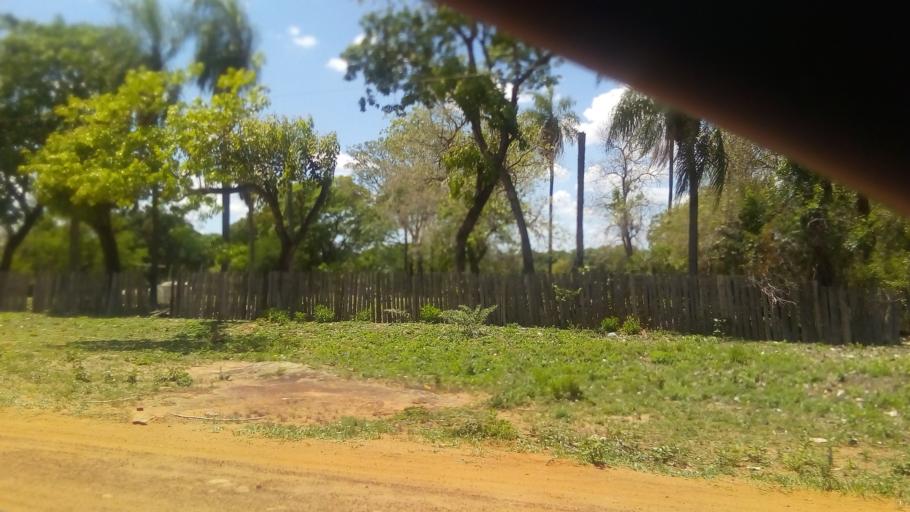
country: PY
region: Cordillera
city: Arroyos y Esteros
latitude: -24.9958
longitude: -57.2158
